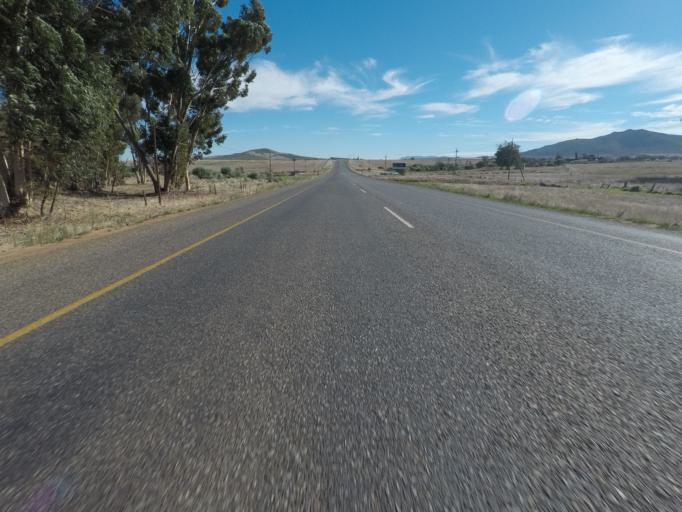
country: ZA
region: Western Cape
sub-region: West Coast District Municipality
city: Malmesbury
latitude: -33.6156
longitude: 18.7269
